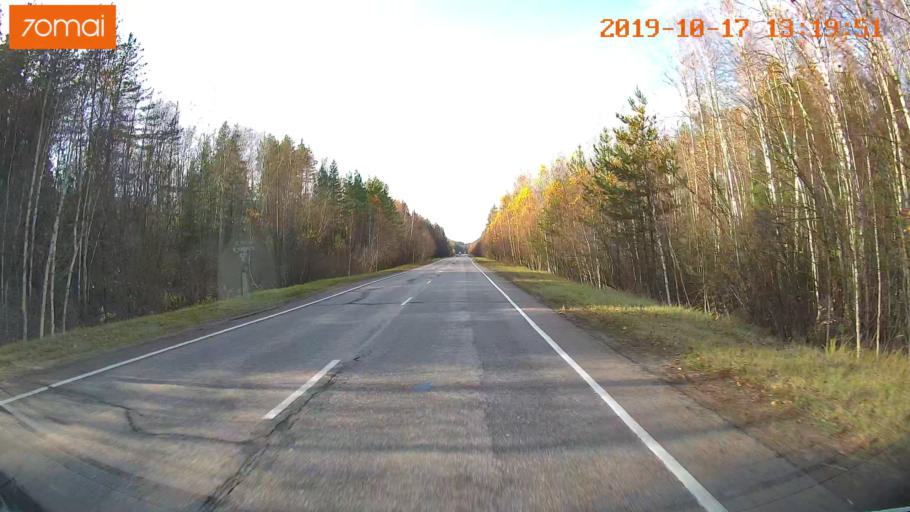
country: RU
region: Rjazan
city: Gus'-Zheleznyy
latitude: 55.0720
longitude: 41.0643
